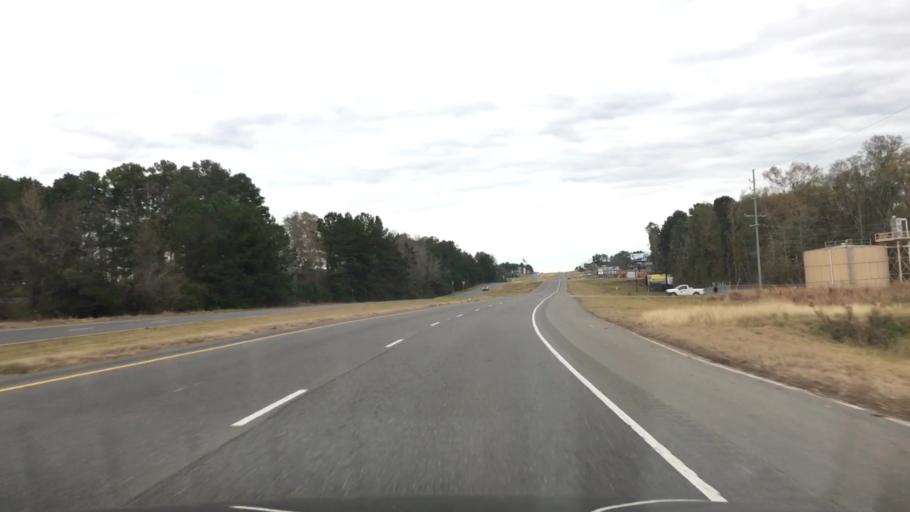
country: US
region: Louisiana
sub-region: Vernon Parish
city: New Llano
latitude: 31.0993
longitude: -93.2693
